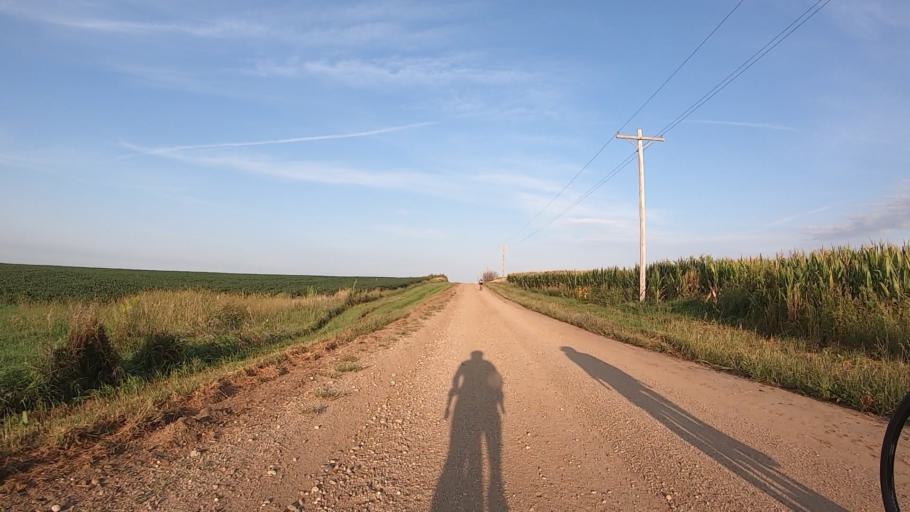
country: US
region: Kansas
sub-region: Marshall County
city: Marysville
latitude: 39.7694
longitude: -96.7400
